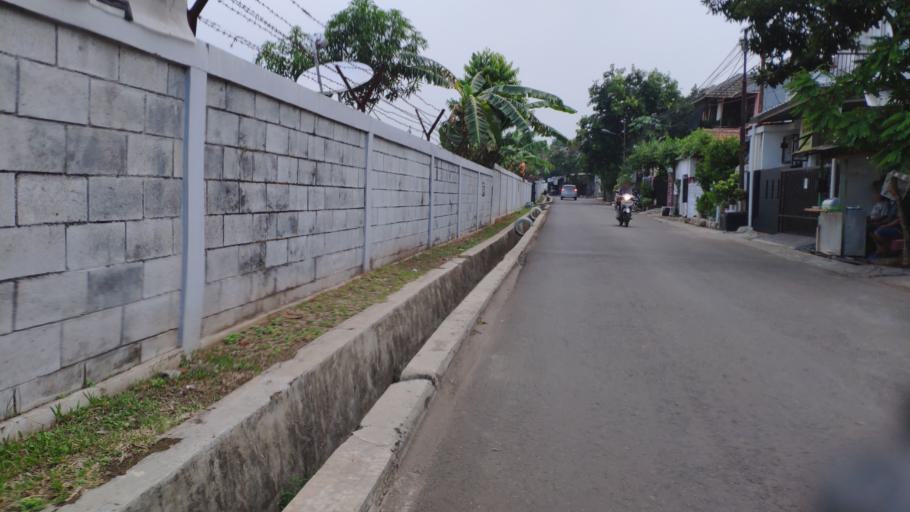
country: ID
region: West Java
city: Pamulang
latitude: -6.2960
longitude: 106.8115
